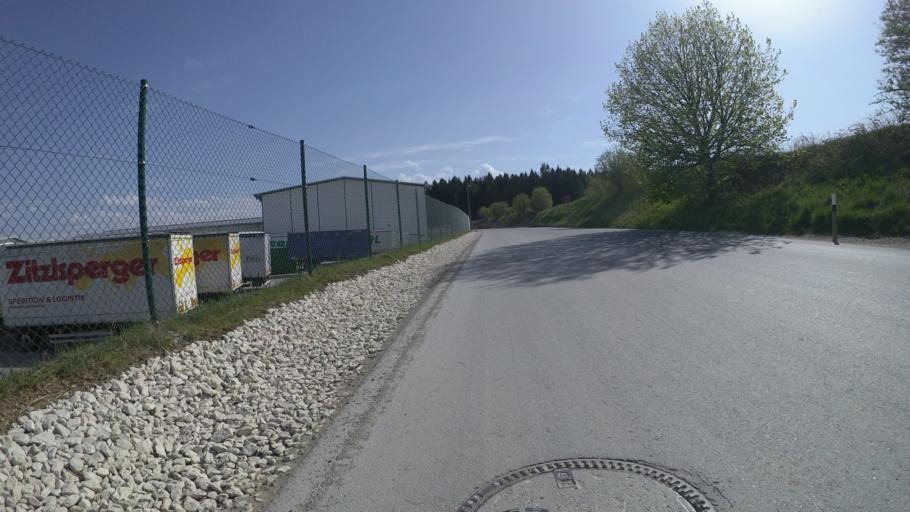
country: DE
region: Bavaria
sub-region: Upper Bavaria
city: Nussdorf
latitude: 47.9058
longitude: 12.6139
